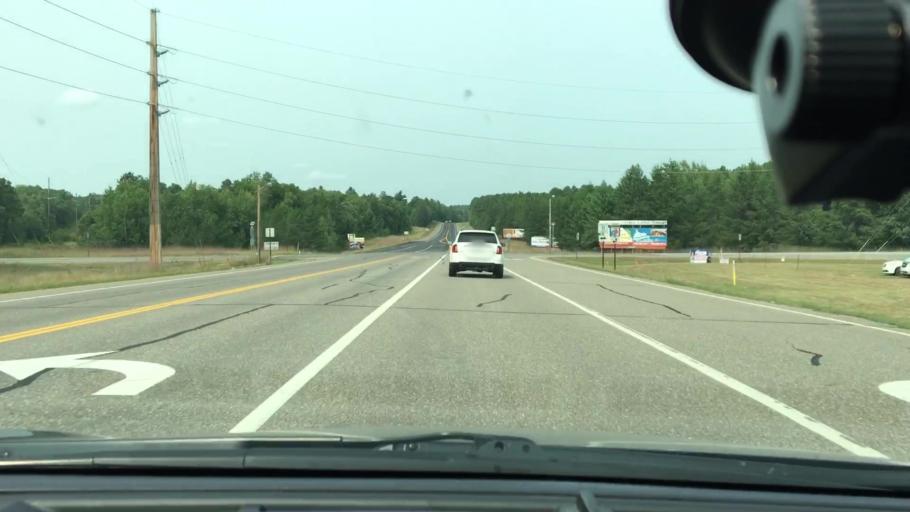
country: US
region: Minnesota
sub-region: Crow Wing County
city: Cross Lake
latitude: 46.6162
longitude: -94.1318
